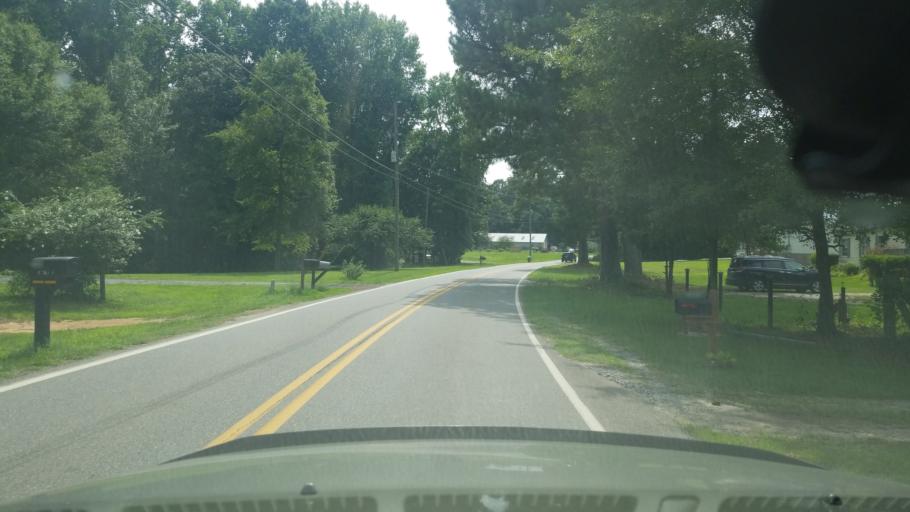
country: US
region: Georgia
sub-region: Forsyth County
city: Cumming
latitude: 34.2704
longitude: -84.1709
